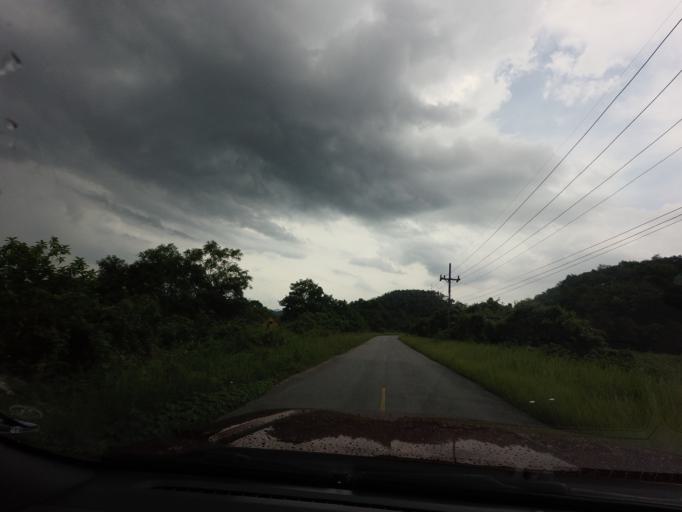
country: TH
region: Yala
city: Ban Nang Sata
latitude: 6.2221
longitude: 101.2282
